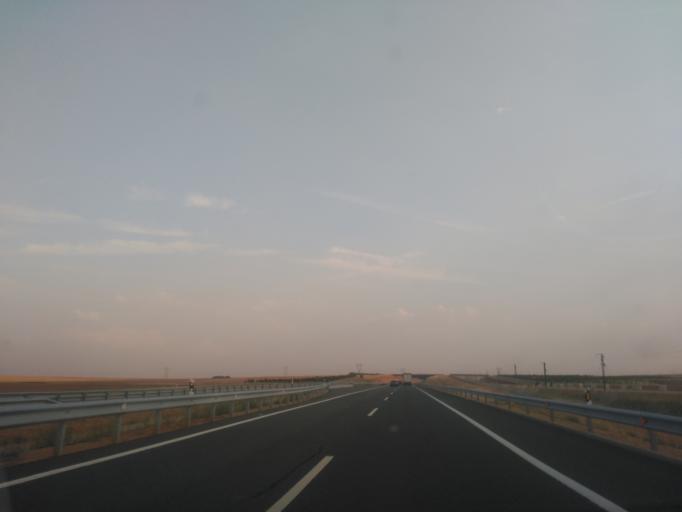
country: ES
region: Castille and Leon
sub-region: Provincia de Zamora
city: Montamarta
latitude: 41.6667
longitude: -5.8004
